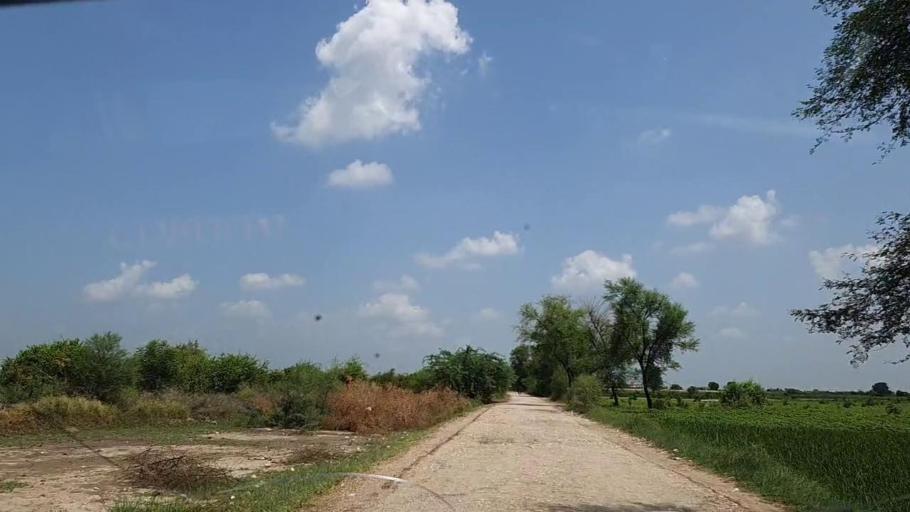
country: PK
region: Sindh
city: Tharu Shah
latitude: 26.9979
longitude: 68.0680
